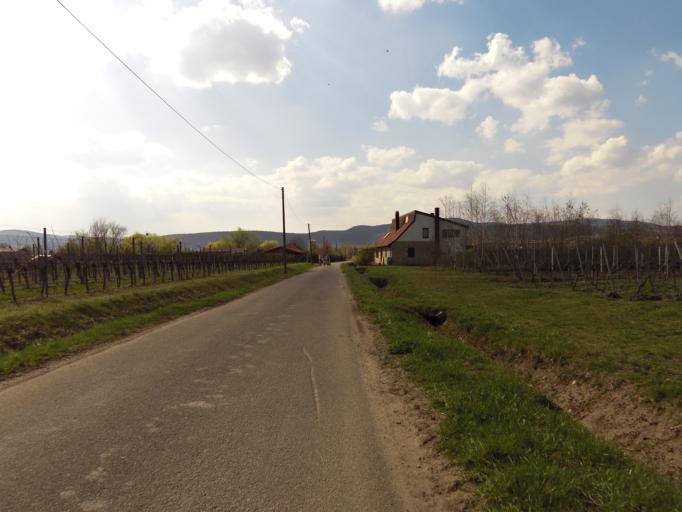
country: DE
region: Rheinland-Pfalz
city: Kallstadt
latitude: 49.4775
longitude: 8.1970
